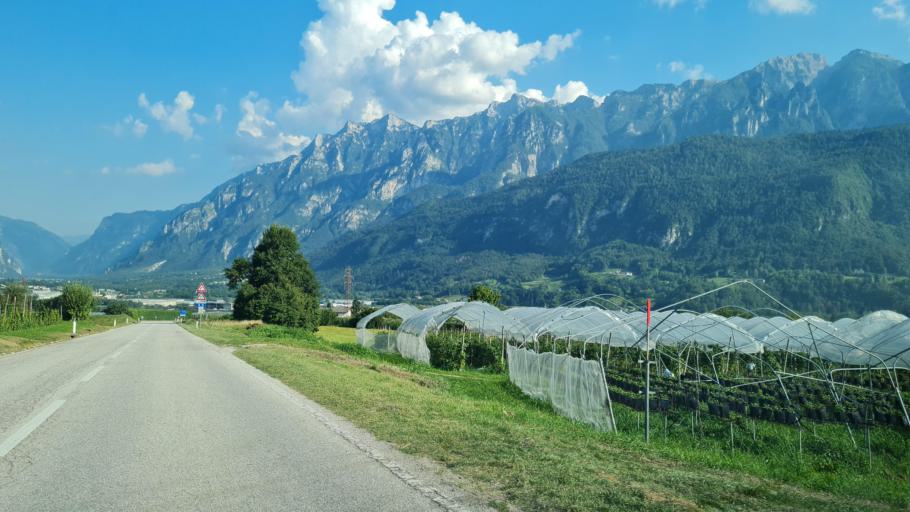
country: IT
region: Trentino-Alto Adige
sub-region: Provincia di Trento
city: Castelnuovo
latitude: 46.0632
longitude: 11.4875
